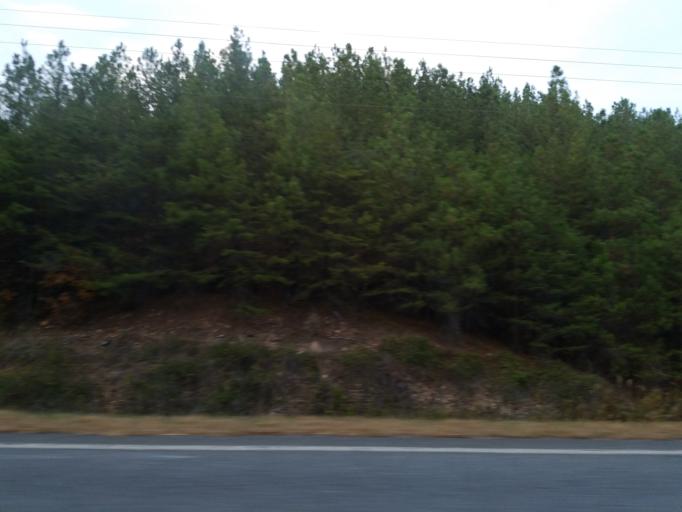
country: US
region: Georgia
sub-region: Murray County
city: Chatsworth
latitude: 34.5920
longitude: -84.7281
